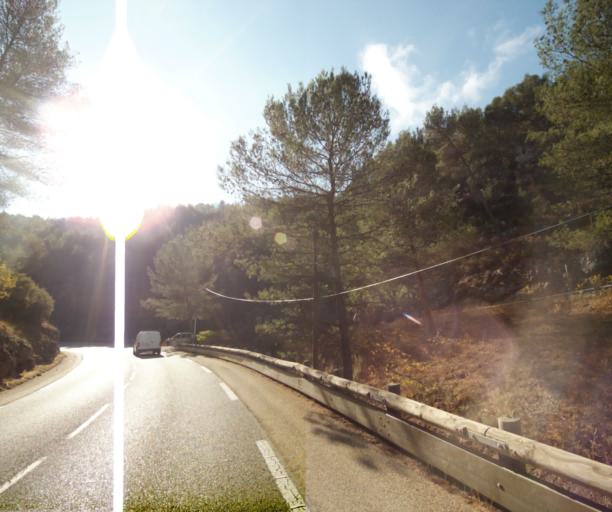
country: FR
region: Provence-Alpes-Cote d'Azur
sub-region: Departement des Bouches-du-Rhone
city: Saint-Savournin
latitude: 43.3682
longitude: 5.5122
